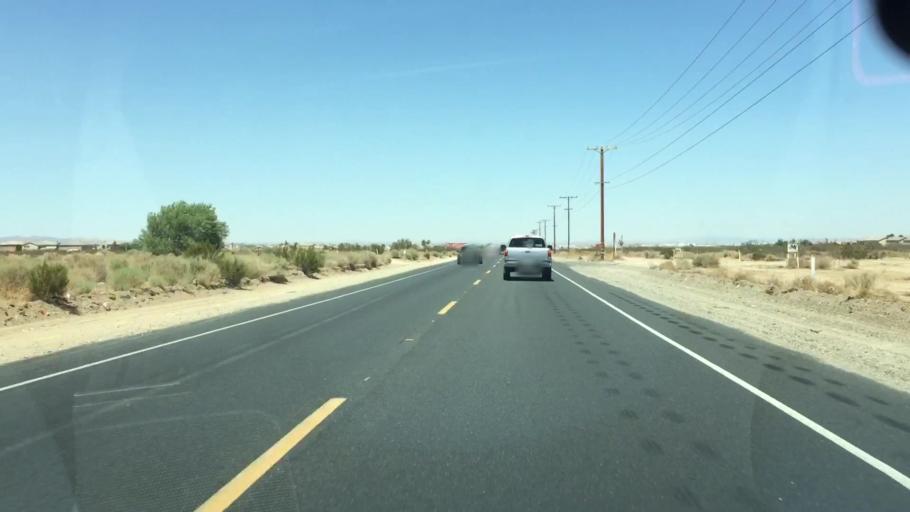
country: US
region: California
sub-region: San Bernardino County
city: Mountain View Acres
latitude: 34.4843
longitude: -117.3995
